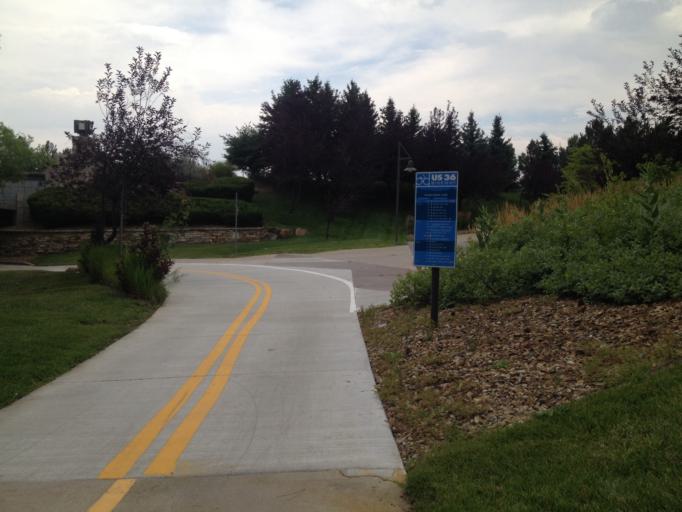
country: US
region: Colorado
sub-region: Broomfield County
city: Broomfield
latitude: 39.9332
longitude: -105.1286
